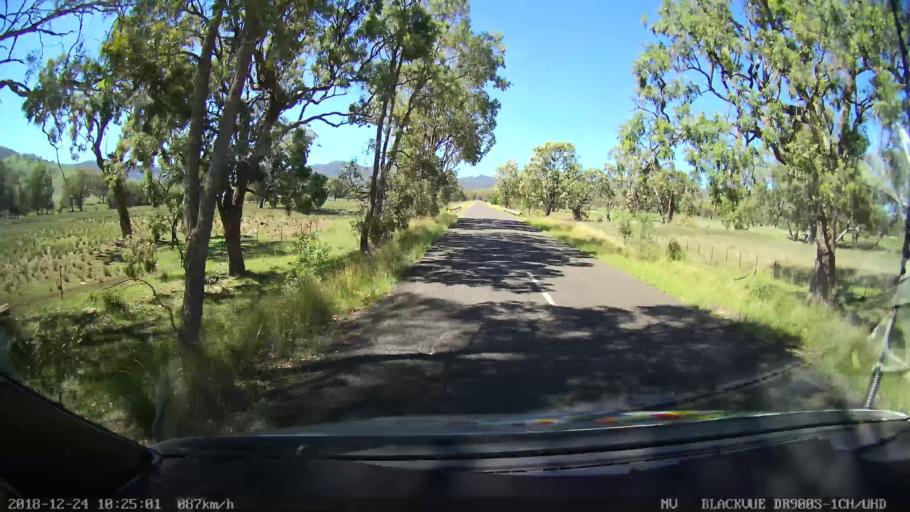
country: AU
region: New South Wales
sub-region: Liverpool Plains
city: Quirindi
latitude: -31.7937
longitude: 150.5303
